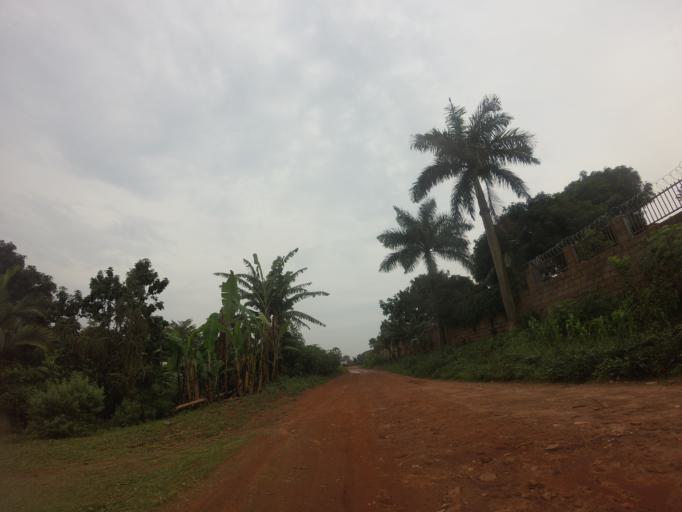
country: UG
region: Central Region
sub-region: Wakiso District
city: Kireka
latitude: 0.3517
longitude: 32.6222
